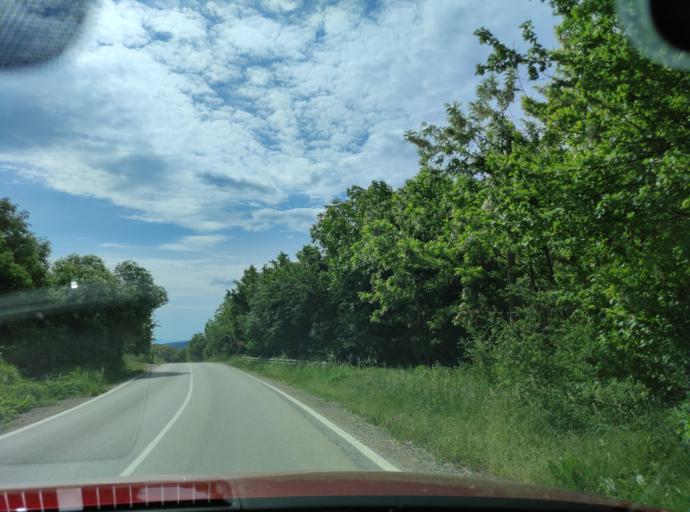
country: BG
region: Montana
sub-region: Obshtina Chiprovtsi
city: Chiprovtsi
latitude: 43.4509
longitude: 22.9085
